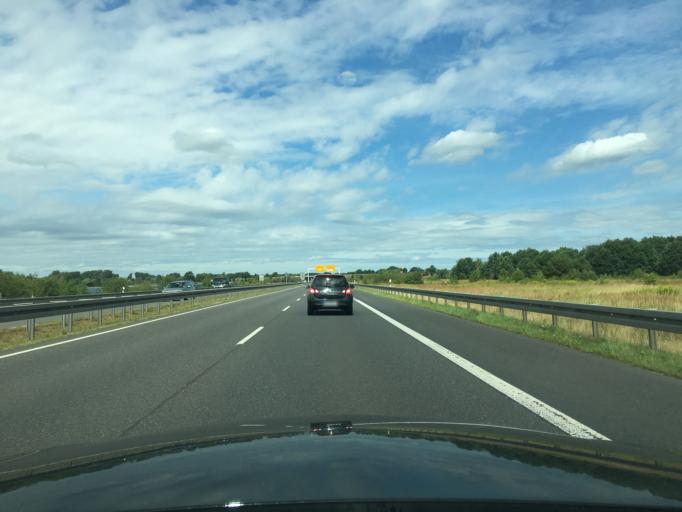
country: DE
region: Brandenburg
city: Leegebruch
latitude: 52.7333
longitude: 13.2117
